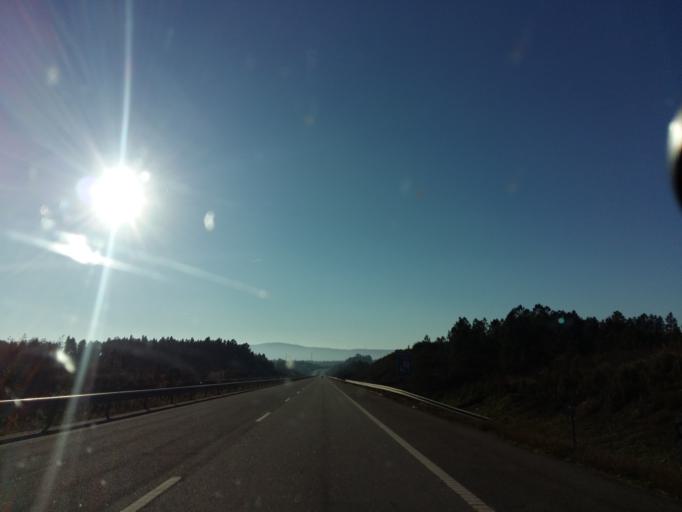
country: ES
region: Extremadura
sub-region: Provincia de Caceres
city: Cedillo
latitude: 39.7404
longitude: -7.6429
